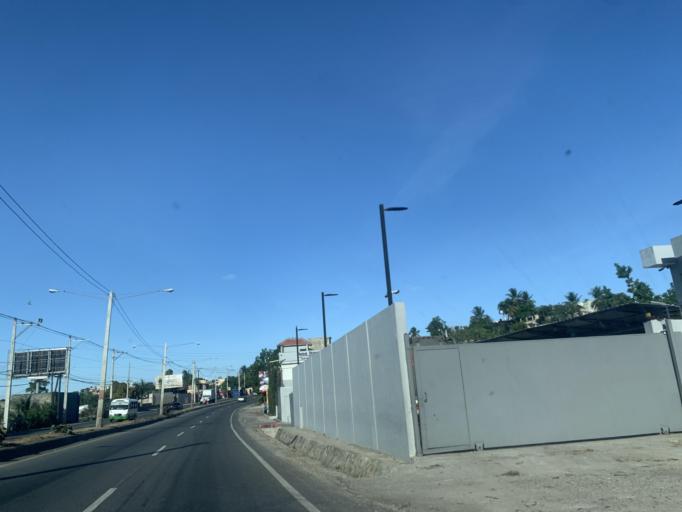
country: DO
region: San Cristobal
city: El Carril
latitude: 18.4358
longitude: -70.0161
